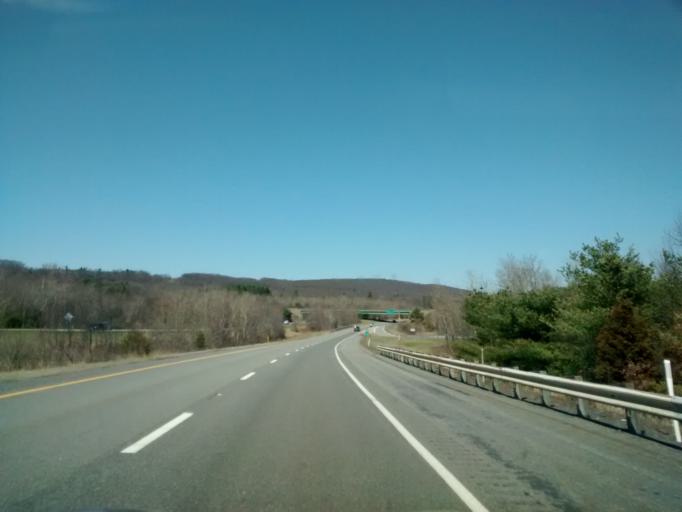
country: US
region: Massachusetts
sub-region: Worcester County
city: Oxford
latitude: 42.1470
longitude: -71.8573
